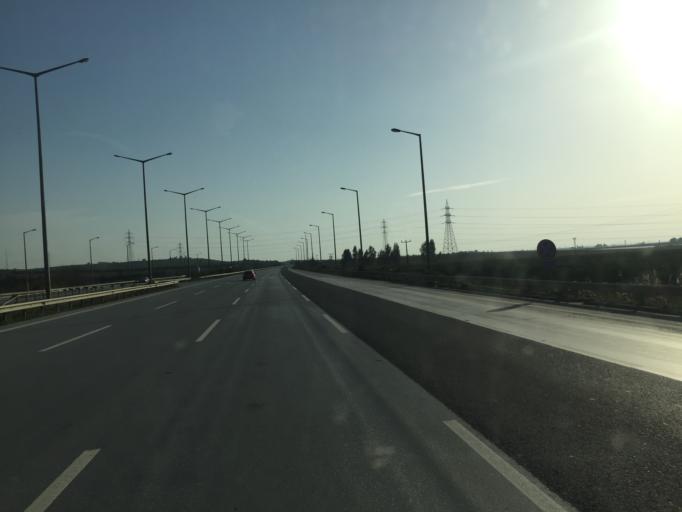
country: TR
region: Mersin
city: Yenice
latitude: 37.0235
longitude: 35.0658
